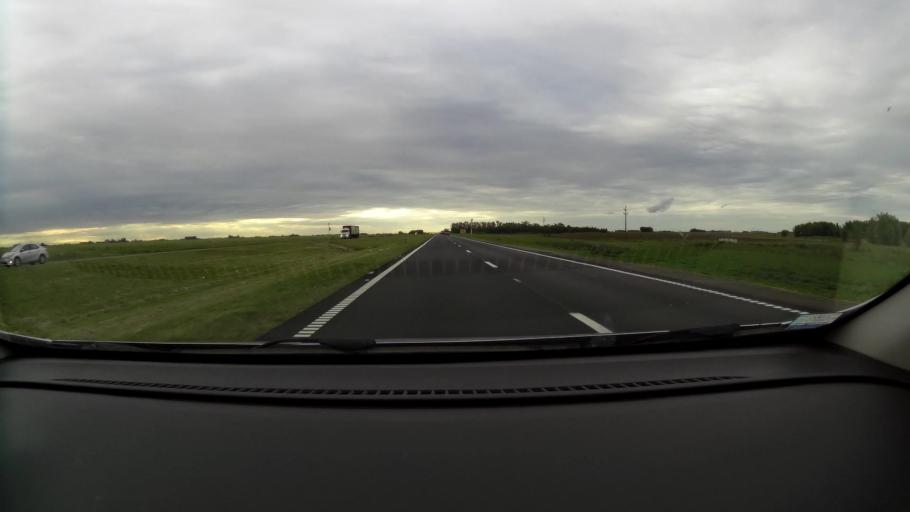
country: AR
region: Buenos Aires
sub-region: Partido de Ramallo
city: Ramallo
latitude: -33.6250
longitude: -60.0017
